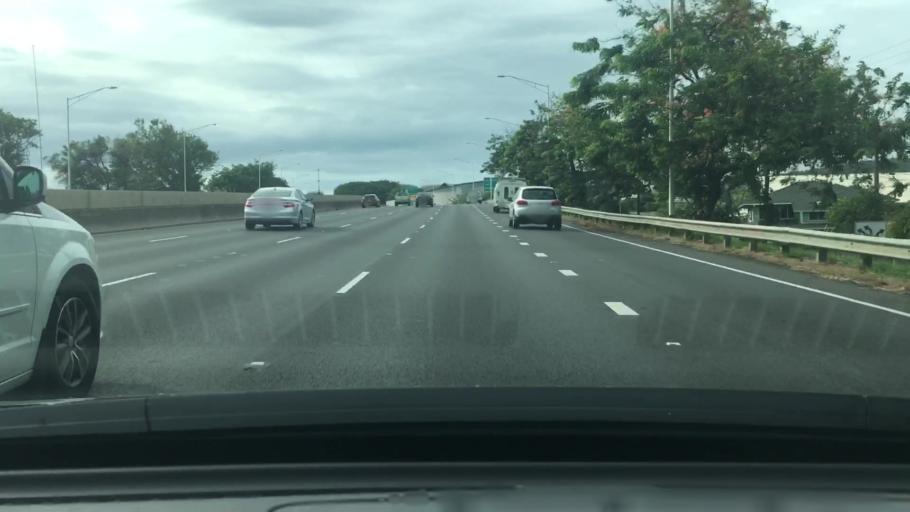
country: US
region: Hawaii
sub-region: Honolulu County
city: Honolulu
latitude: 21.3291
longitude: -157.8691
